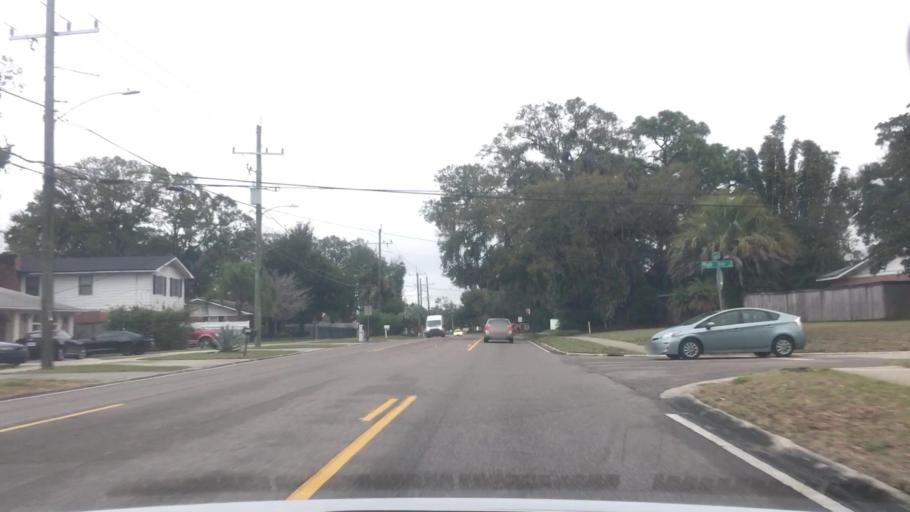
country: US
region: Florida
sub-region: Duval County
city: Jacksonville
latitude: 30.3577
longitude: -81.5778
